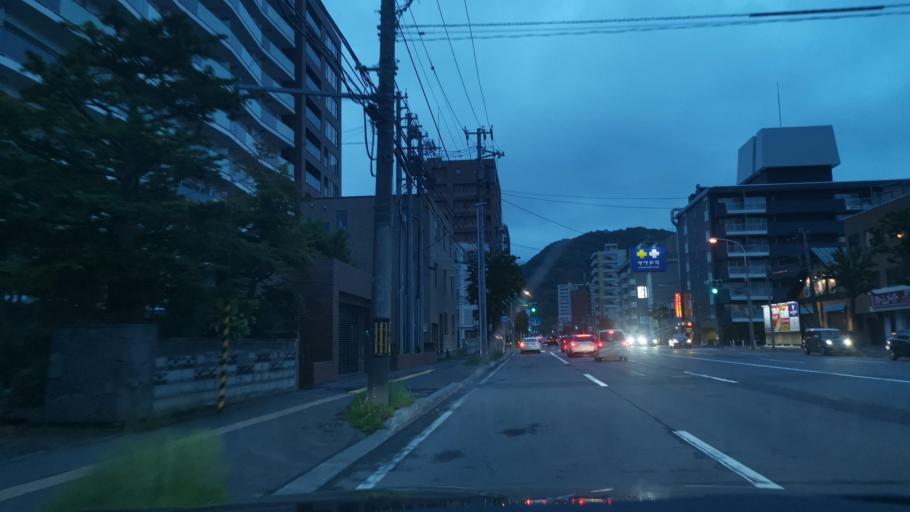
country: JP
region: Hokkaido
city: Sapporo
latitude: 43.0602
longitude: 141.3149
